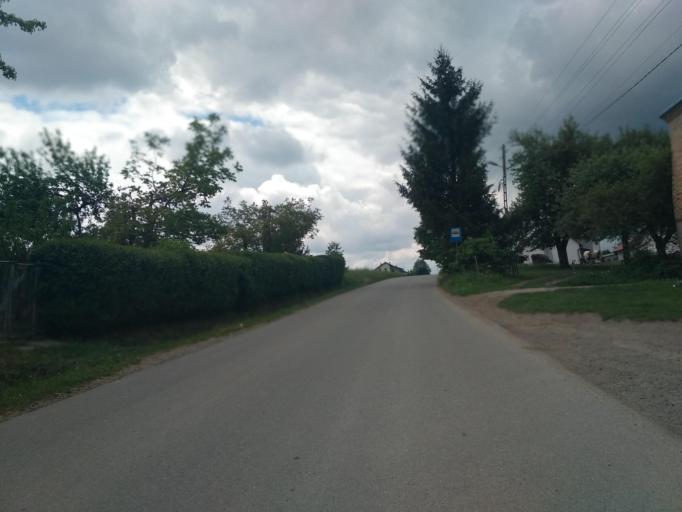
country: PL
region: Subcarpathian Voivodeship
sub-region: Powiat jasielski
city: Tarnowiec
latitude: 49.6672
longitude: 21.5656
